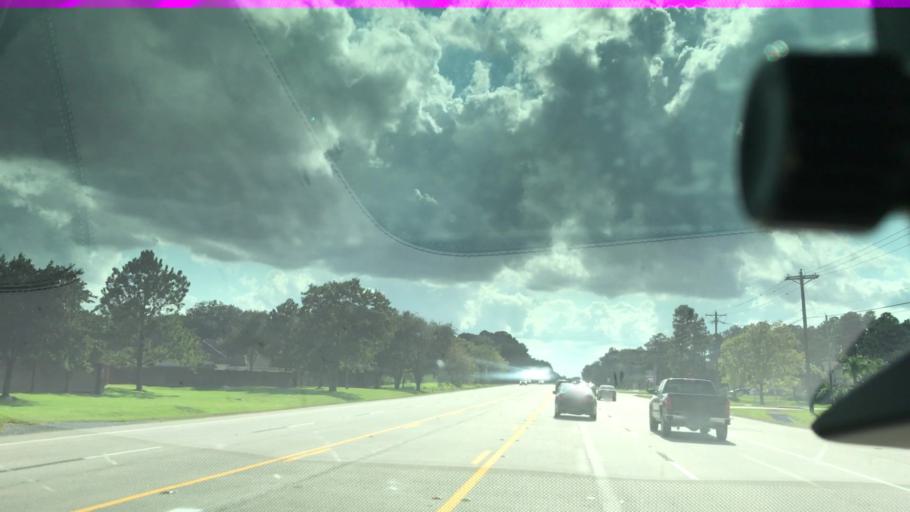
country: US
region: Texas
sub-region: Galveston County
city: League City
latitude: 29.4953
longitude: -95.1407
